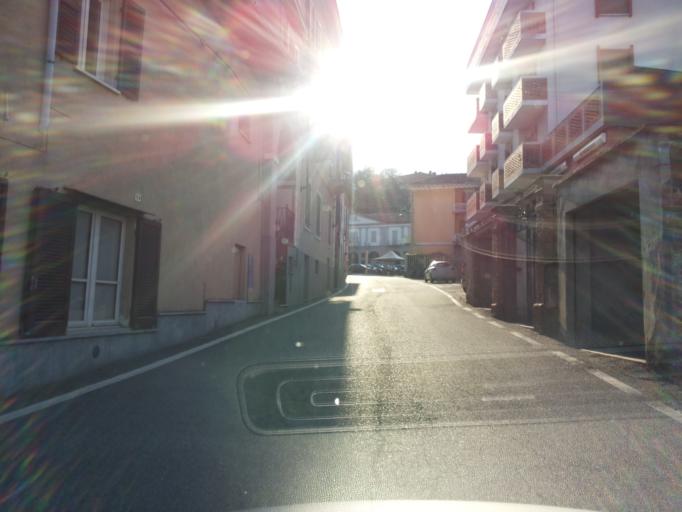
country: IT
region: Piedmont
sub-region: Provincia di Torino
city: Azeglio
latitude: 45.4249
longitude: 7.9964
